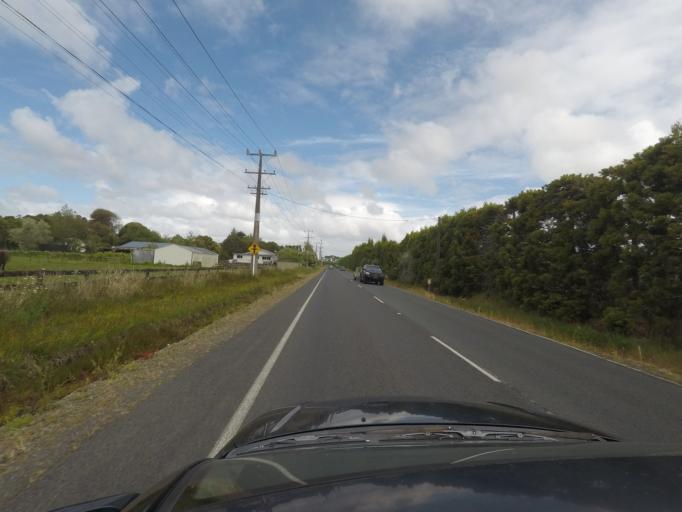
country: NZ
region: Auckland
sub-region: Auckland
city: Muriwai Beach
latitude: -36.7753
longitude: 174.5755
